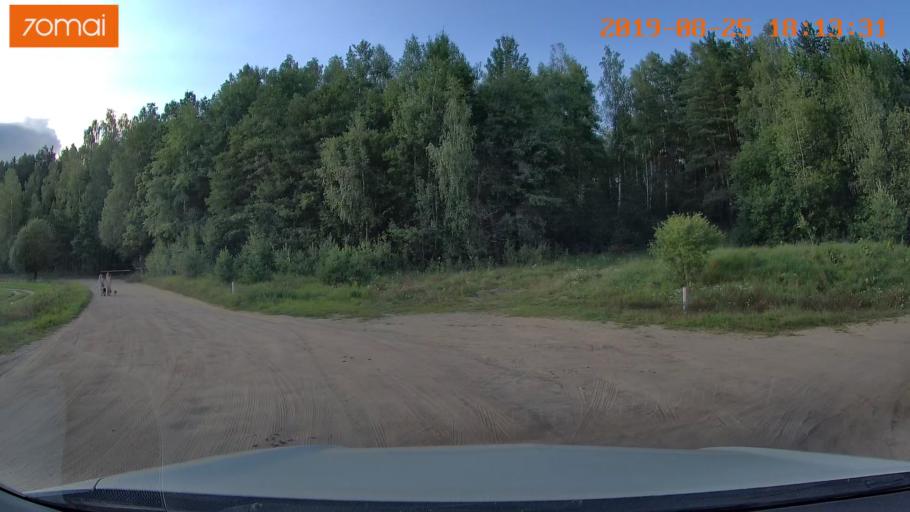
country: BY
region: Minsk
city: Khatsyezhyna
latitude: 53.9442
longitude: 27.3067
